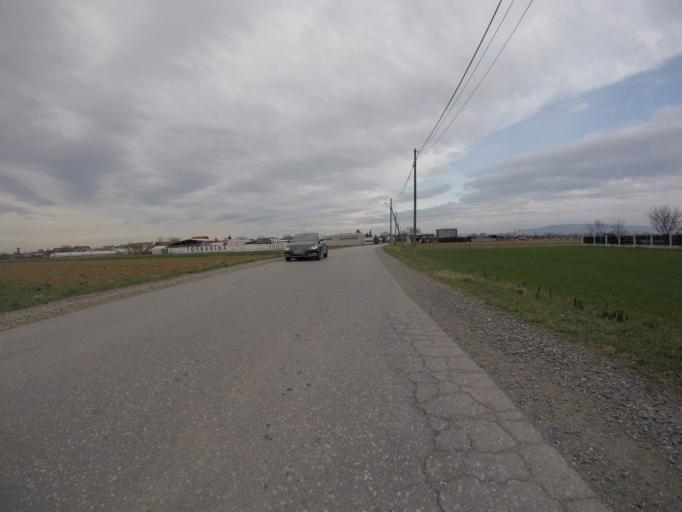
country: HR
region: Zagrebacka
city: Gradici
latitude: 45.7109
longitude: 16.0313
